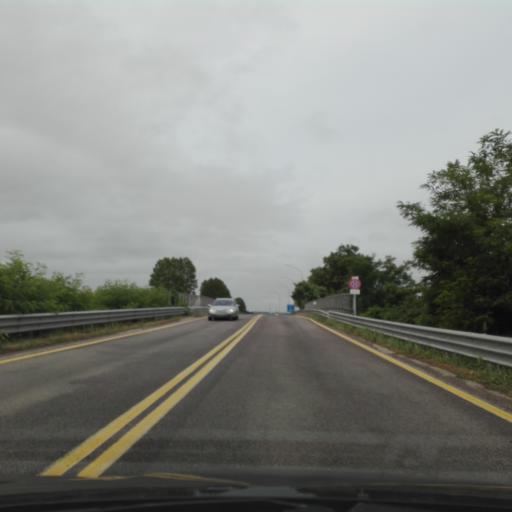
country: IT
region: Veneto
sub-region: Provincia di Rovigo
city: Grignano Polesine
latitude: 45.0796
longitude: 11.7406
